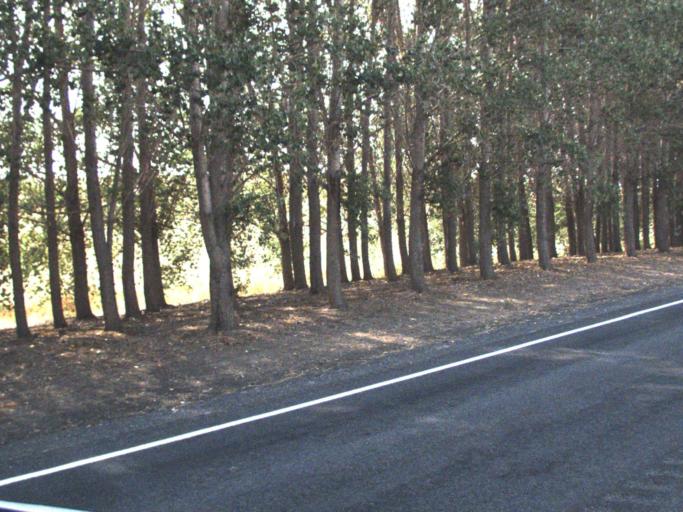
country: US
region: Washington
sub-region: Whitman County
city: Pullman
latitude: 46.8844
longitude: -117.1227
